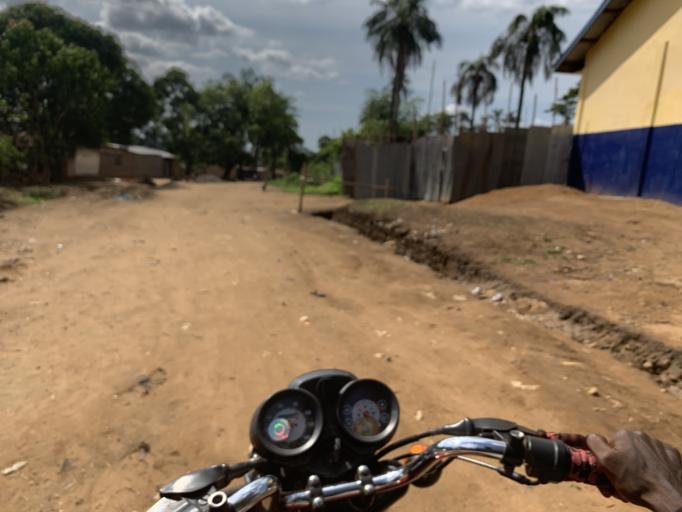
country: SL
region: Western Area
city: Waterloo
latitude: 8.3311
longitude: -13.0639
